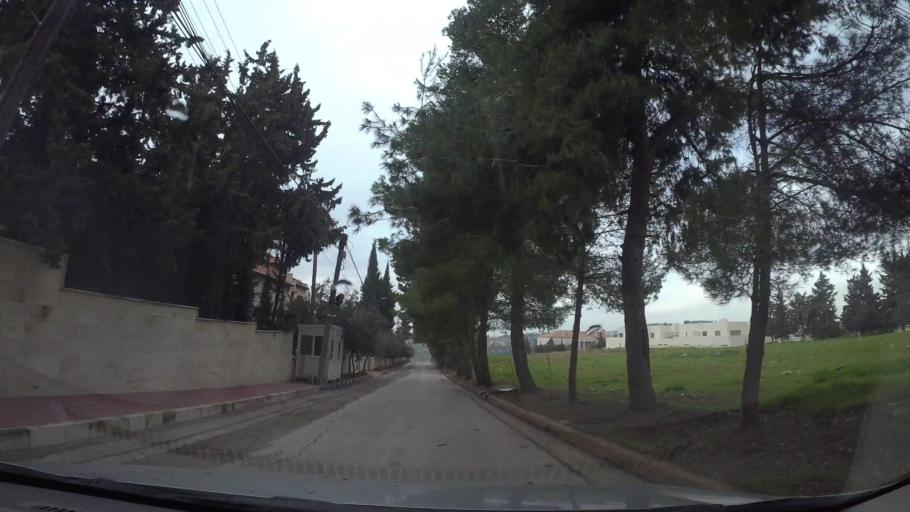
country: JO
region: Amman
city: Wadi as Sir
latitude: 31.9851
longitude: 35.8195
